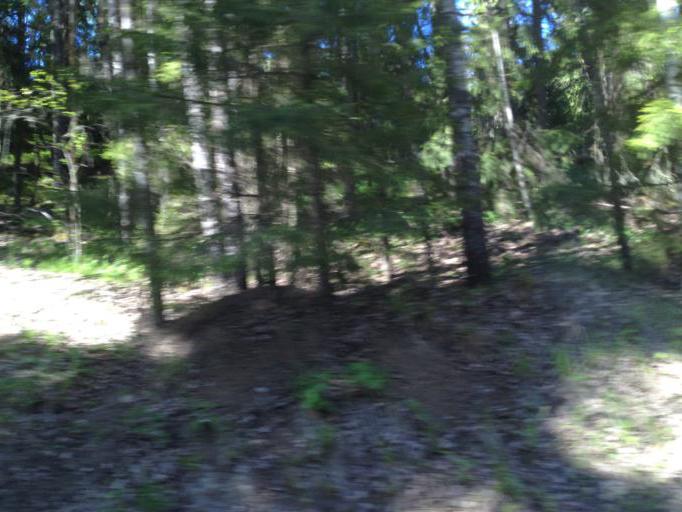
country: FI
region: Uusimaa
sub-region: Helsinki
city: Espoo
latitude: 60.3075
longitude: 24.5329
